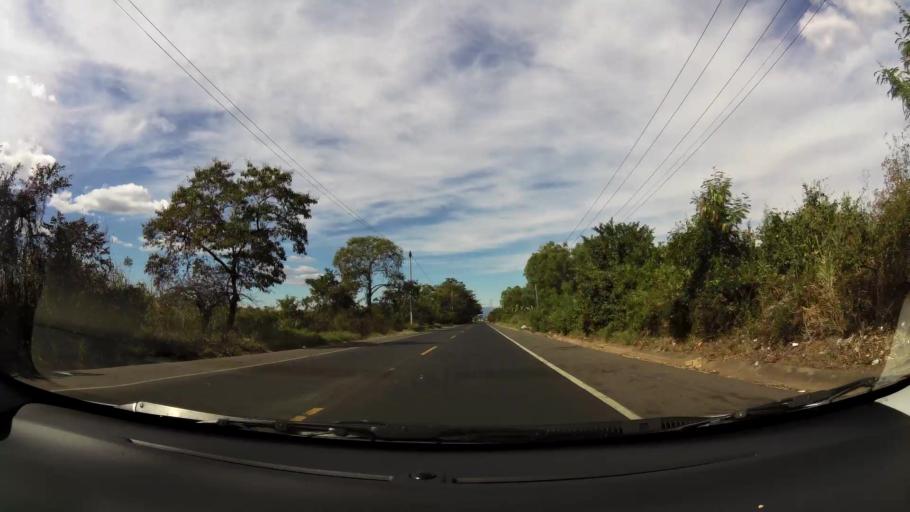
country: SV
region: San Salvador
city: Guazapa
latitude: 13.9029
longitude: -89.1797
